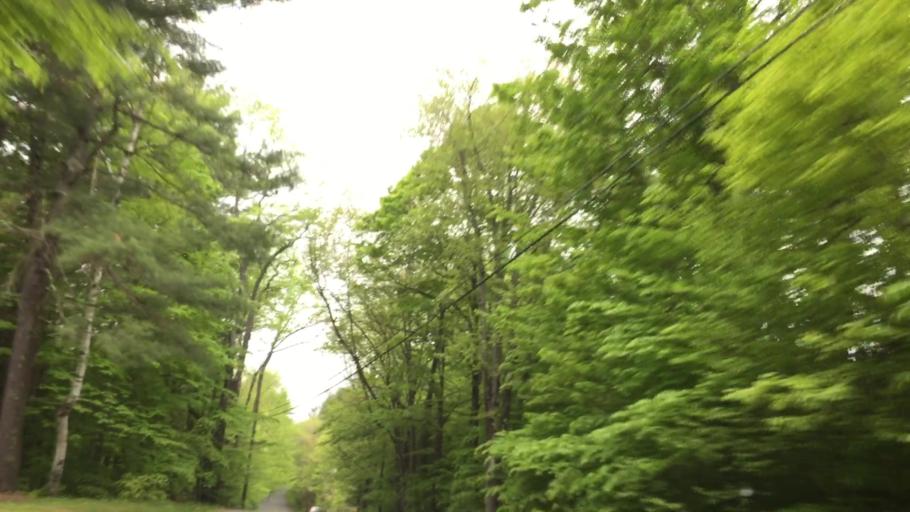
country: US
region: Massachusetts
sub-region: Berkshire County
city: Becket
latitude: 42.2808
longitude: -73.0460
